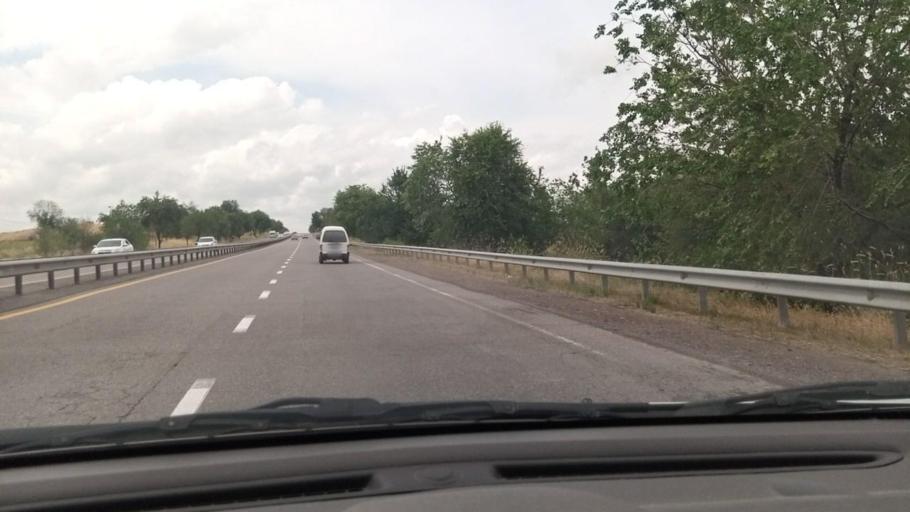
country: UZ
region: Toshkent
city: Ohangaron
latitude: 41.0093
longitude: 69.5203
